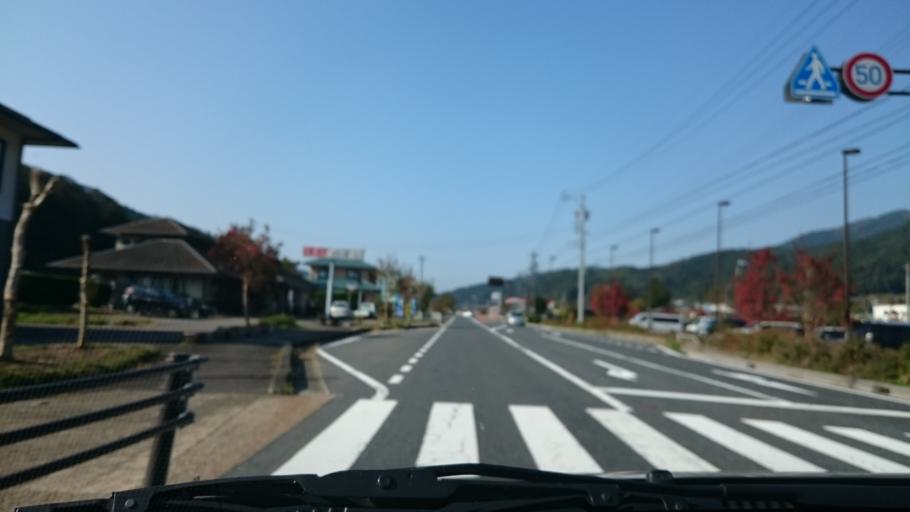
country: JP
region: Gifu
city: Nakatsugawa
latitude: 35.7091
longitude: 137.3747
